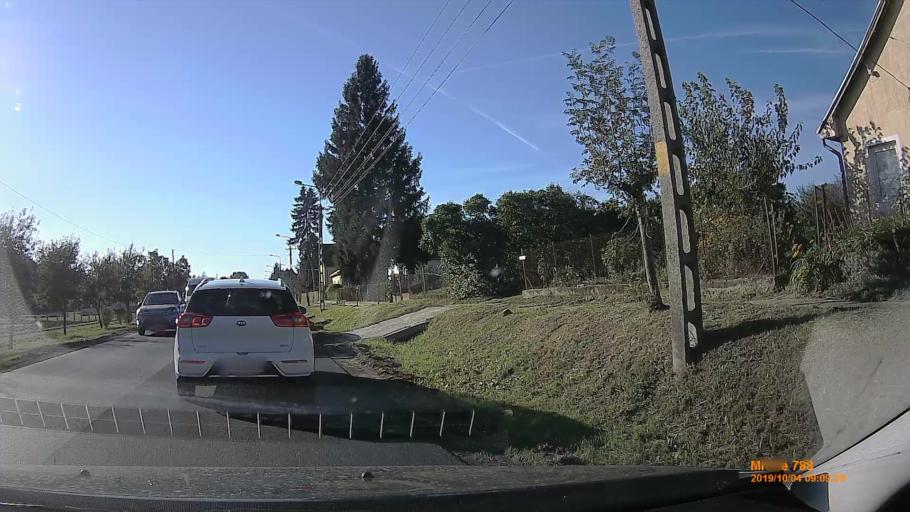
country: HU
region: Somogy
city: Karad
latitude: 46.6645
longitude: 17.7800
